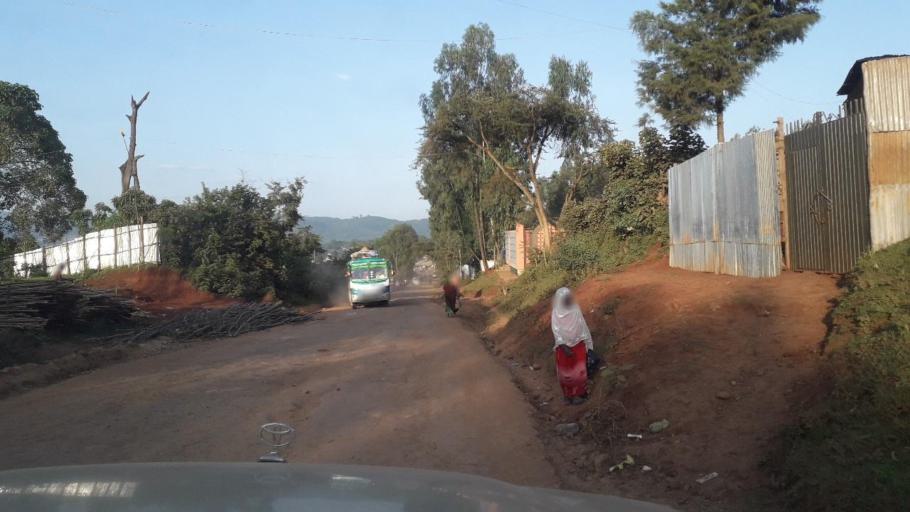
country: ET
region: Oromiya
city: Jima
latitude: 7.6386
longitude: 36.8385
